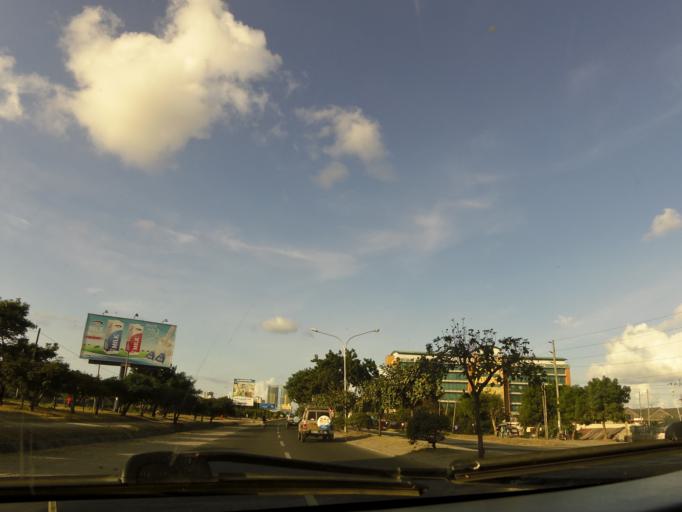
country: TZ
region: Dar es Salaam
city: Dar es Salaam
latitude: -6.8314
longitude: 39.2692
